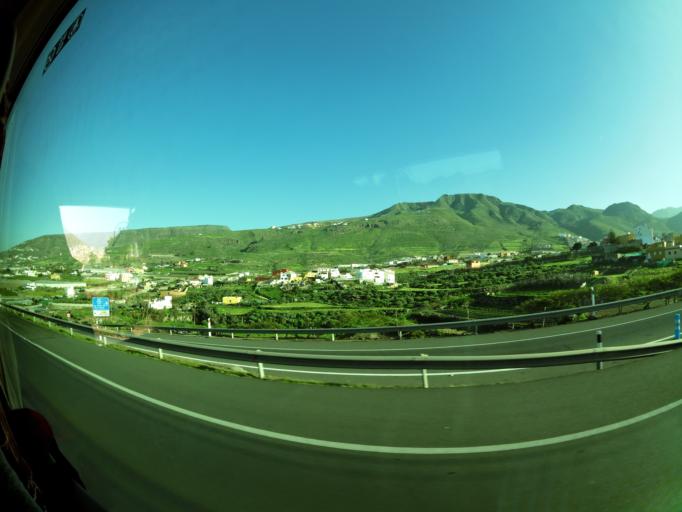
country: ES
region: Canary Islands
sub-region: Provincia de Las Palmas
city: Galdar
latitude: 28.1247
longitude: -15.6649
